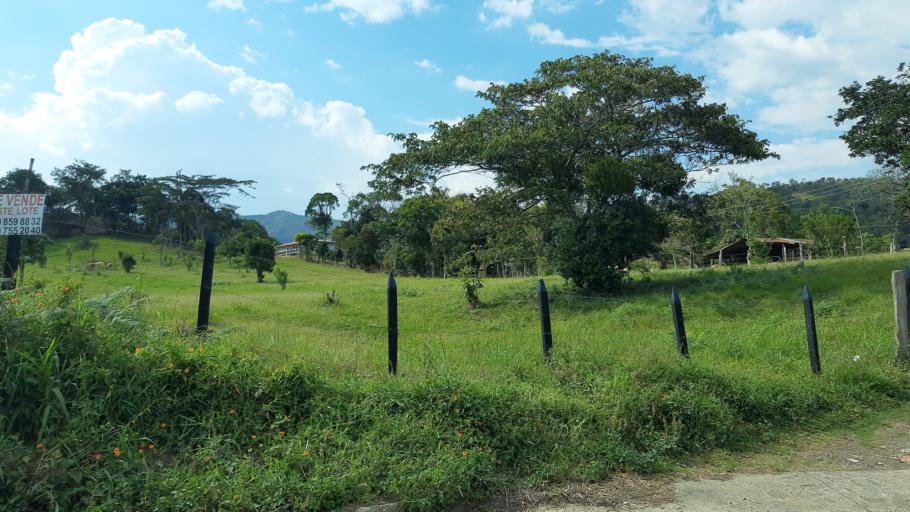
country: CO
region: Boyaca
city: Moniquira
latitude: 5.8439
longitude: -73.5812
